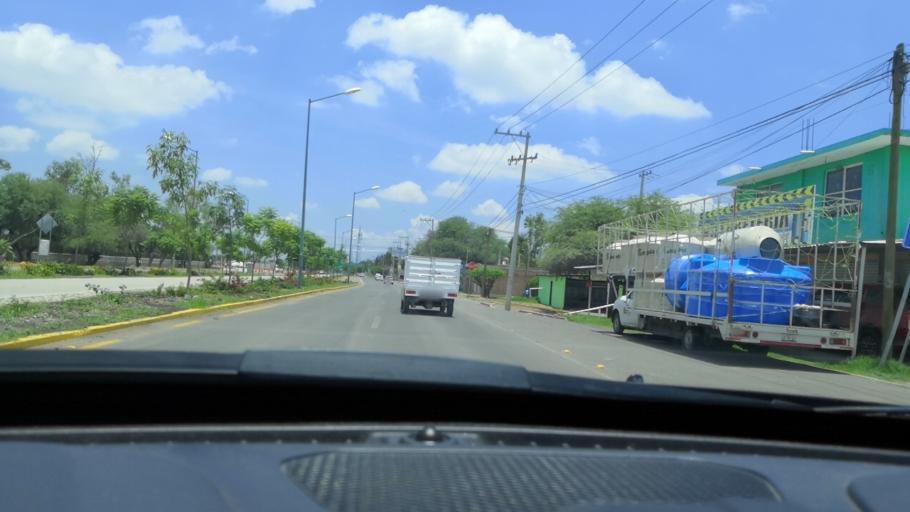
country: MX
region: Guanajuato
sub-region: Silao de la Victoria
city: El Refugio de los Sauces
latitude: 21.0266
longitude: -101.5762
